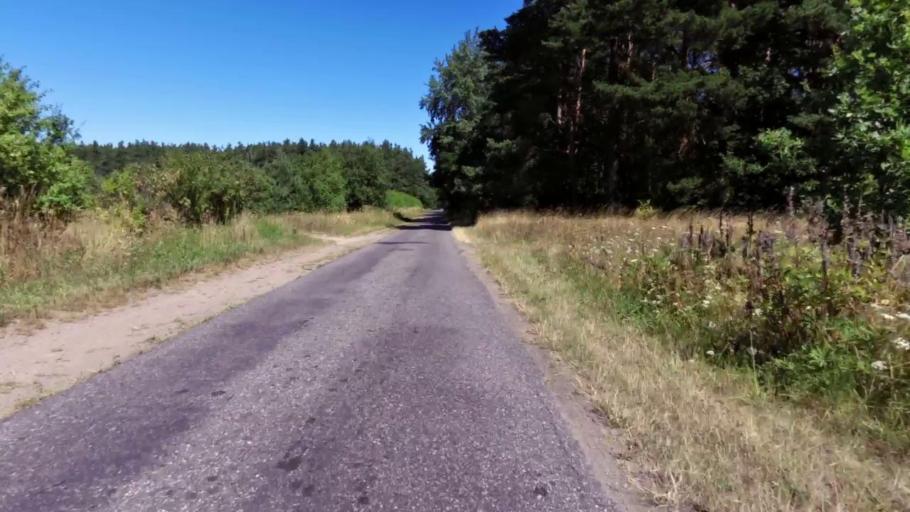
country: PL
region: West Pomeranian Voivodeship
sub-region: Powiat szczecinecki
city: Szczecinek
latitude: 53.6441
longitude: 16.7161
